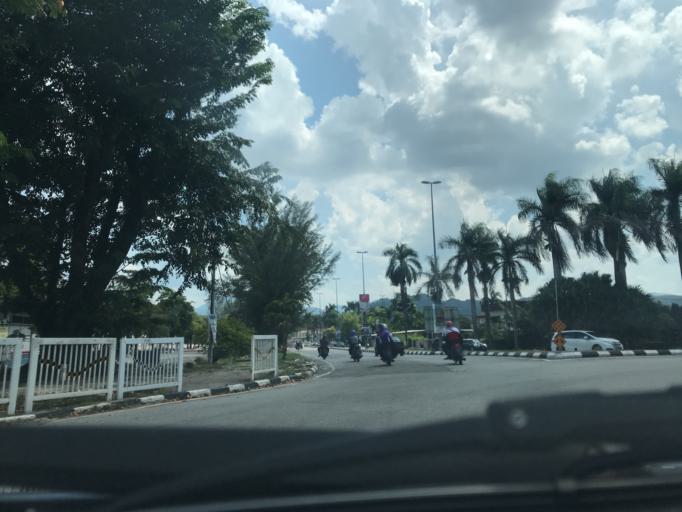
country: MY
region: Perak
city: Ipoh
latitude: 4.6115
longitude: 101.1045
